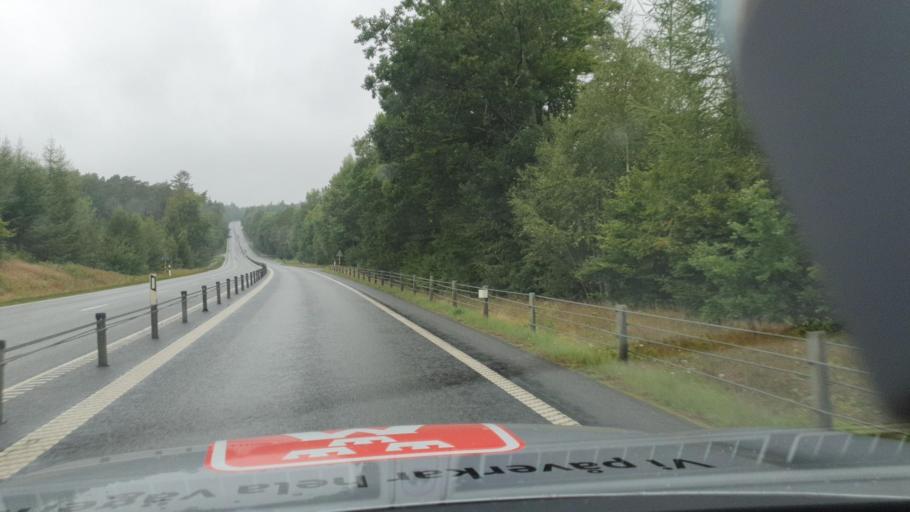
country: SE
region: Skane
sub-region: Ostra Goinge Kommun
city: Broby
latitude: 56.2639
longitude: 14.0476
